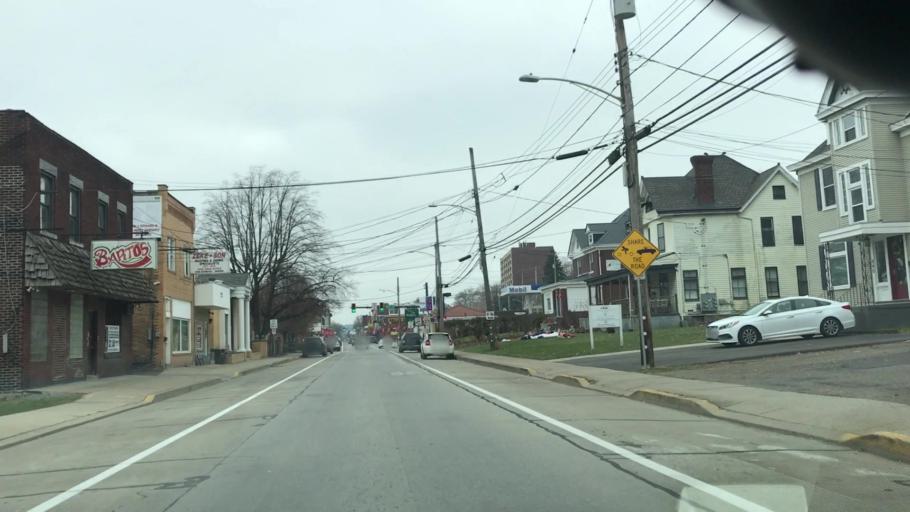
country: US
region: Pennsylvania
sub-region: Allegheny County
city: Coraopolis
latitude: 40.5189
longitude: -80.1680
